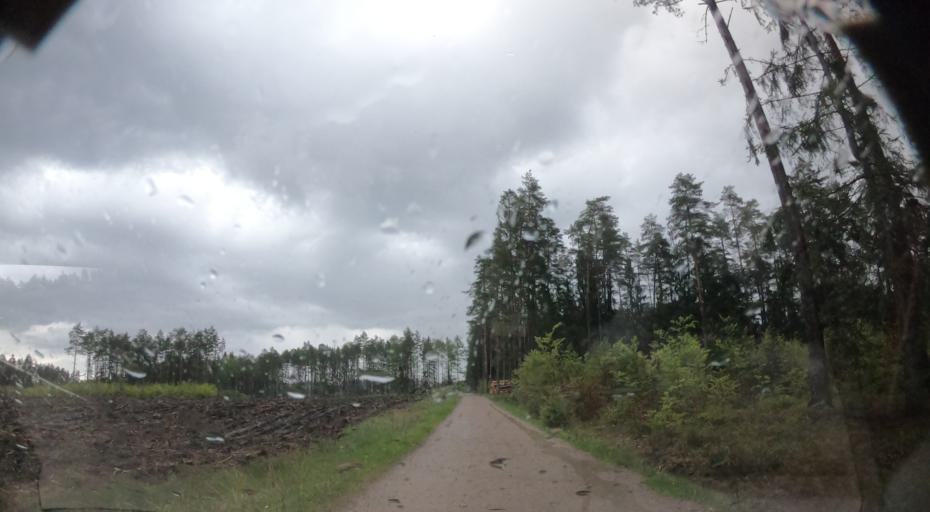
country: PL
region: West Pomeranian Voivodeship
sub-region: Powiat koszalinski
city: Polanow
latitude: 54.1411
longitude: 16.4853
